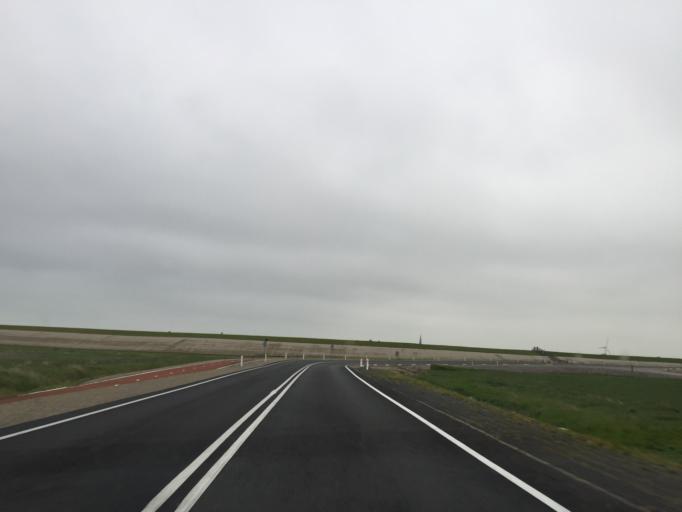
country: NL
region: Friesland
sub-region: Gemeente Dongeradeel
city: Holwerd
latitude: 53.3821
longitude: 5.8912
